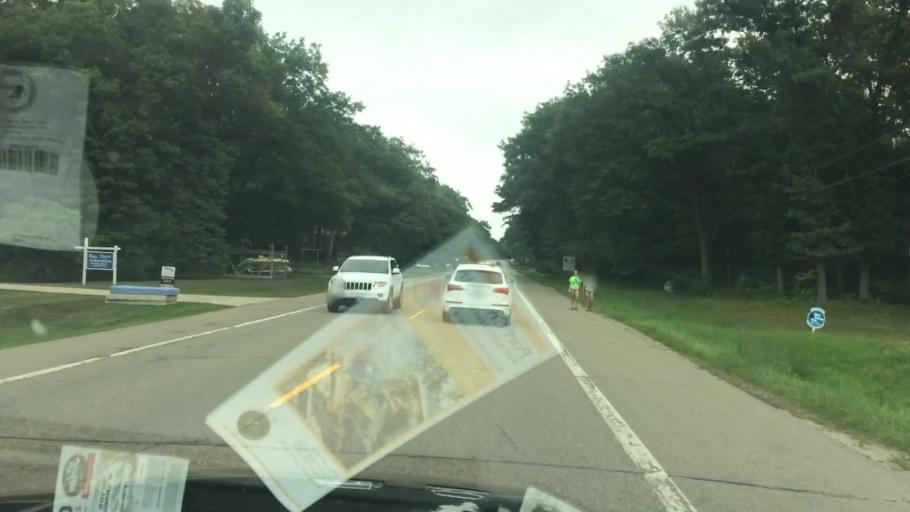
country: US
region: Michigan
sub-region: Huron County
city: Pigeon
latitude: 43.9810
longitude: -83.2052
